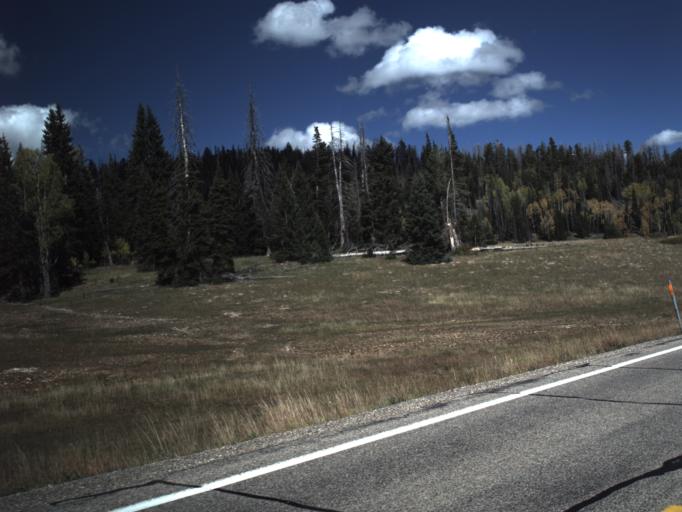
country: US
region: Utah
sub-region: Iron County
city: Cedar City
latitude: 37.5713
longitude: -112.8401
